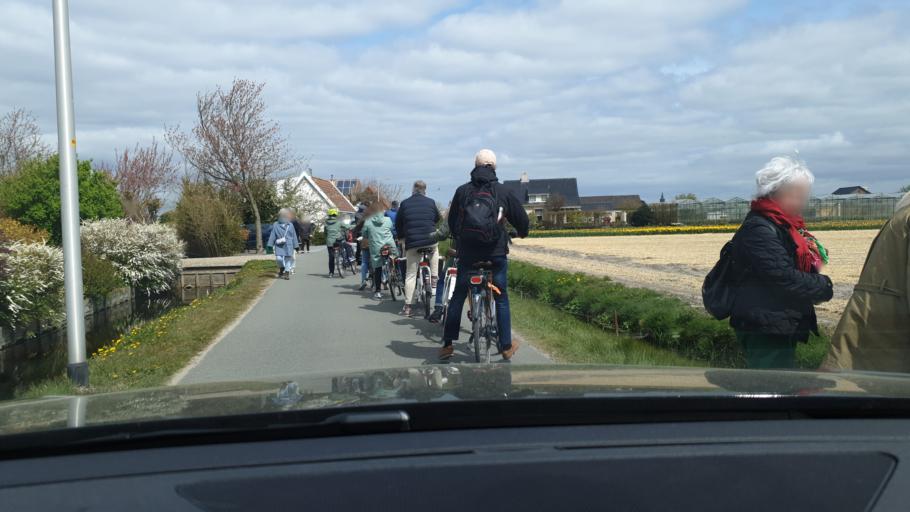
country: NL
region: South Holland
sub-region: Gemeente Lisse
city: Lisse
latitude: 52.2923
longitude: 4.5356
